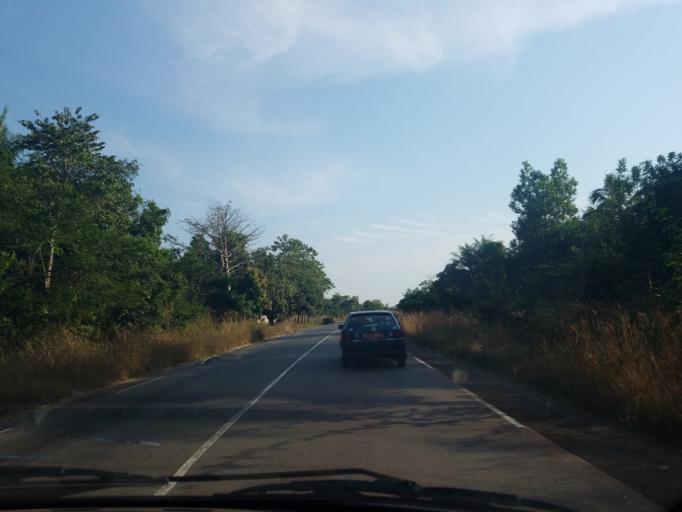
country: GN
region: Boke
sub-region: Boke Prefecture
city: Sangueya
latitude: 10.5102
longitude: -14.4056
